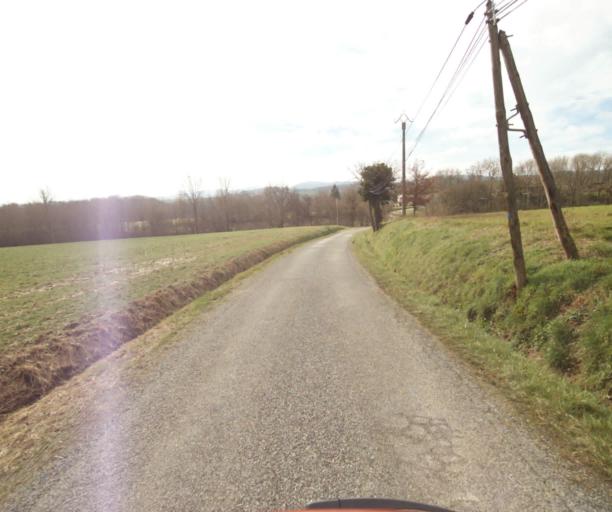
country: FR
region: Midi-Pyrenees
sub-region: Departement de l'Ariege
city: Pamiers
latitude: 43.1062
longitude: 1.5348
